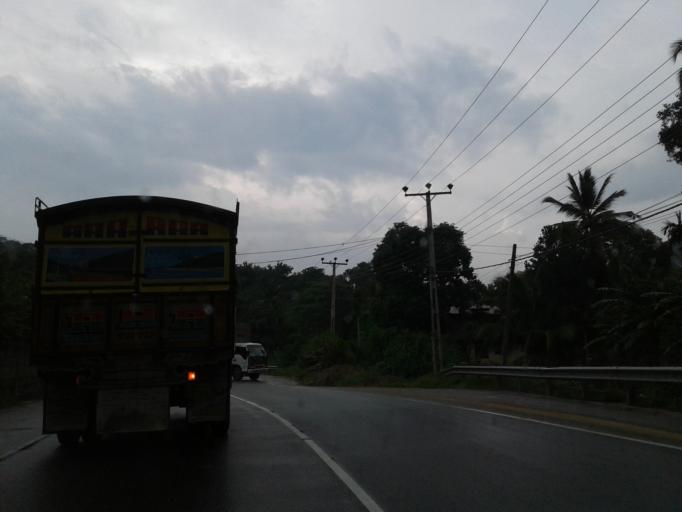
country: LK
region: Central
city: Kadugannawa
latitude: 7.2483
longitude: 80.3392
